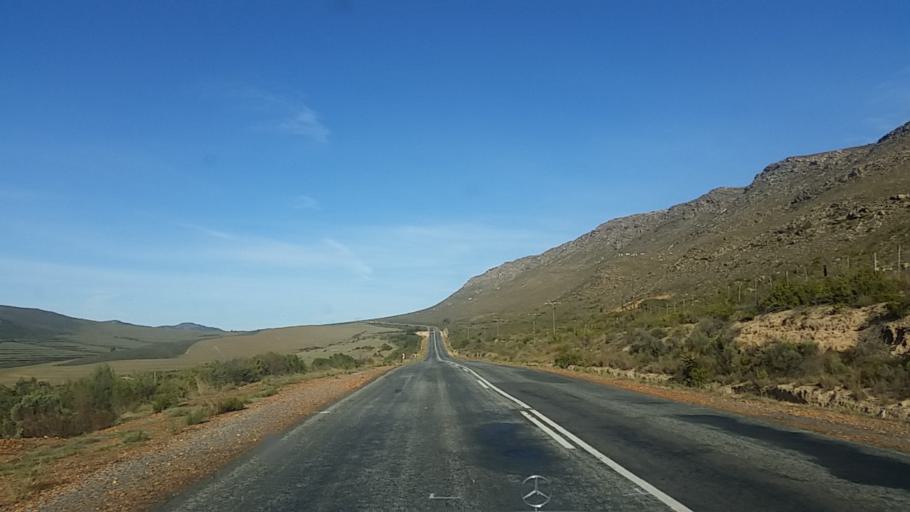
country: ZA
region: Western Cape
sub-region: Eden District Municipality
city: Knysna
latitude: -33.7425
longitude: 23.0098
